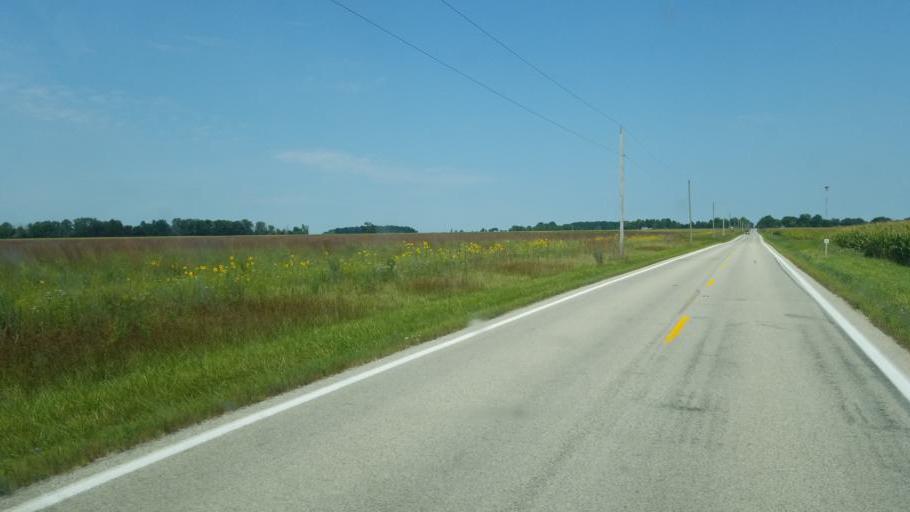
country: US
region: Ohio
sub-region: Marion County
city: Marion
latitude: 40.5971
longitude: -83.2175
